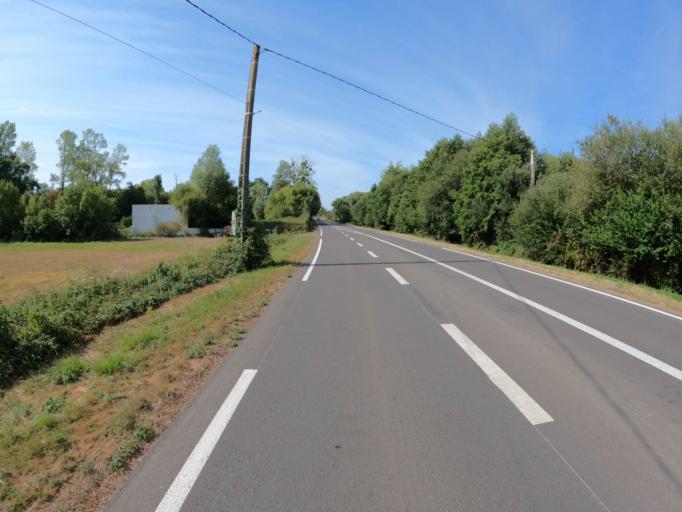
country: FR
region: Pays de la Loire
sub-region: Departement de la Vendee
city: Saint-Christophe-du-Ligneron
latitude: 46.8123
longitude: -1.7729
